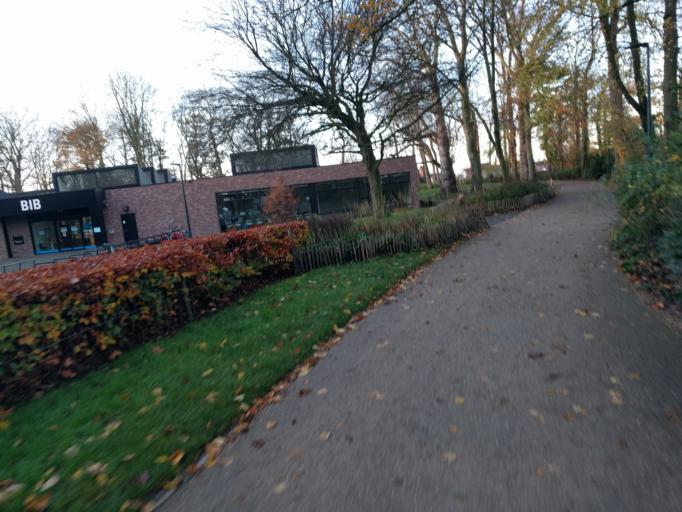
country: BE
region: Flanders
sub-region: Provincie West-Vlaanderen
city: Wevelgem
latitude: 50.8096
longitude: 3.1798
